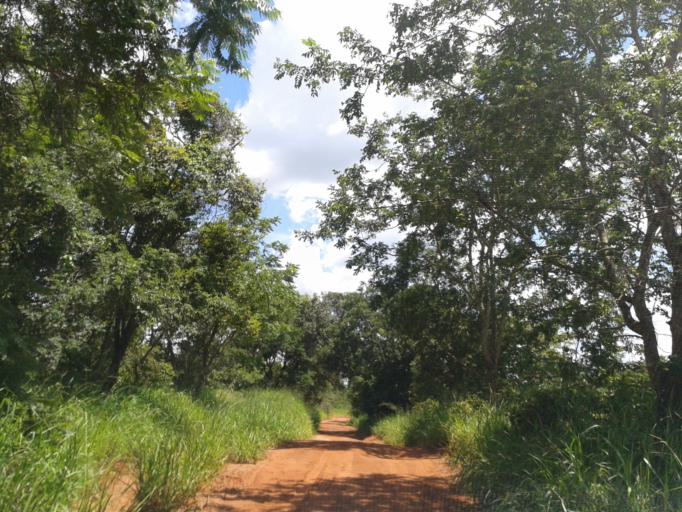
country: BR
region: Minas Gerais
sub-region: Ituiutaba
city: Ituiutaba
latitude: -18.8514
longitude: -49.5009
